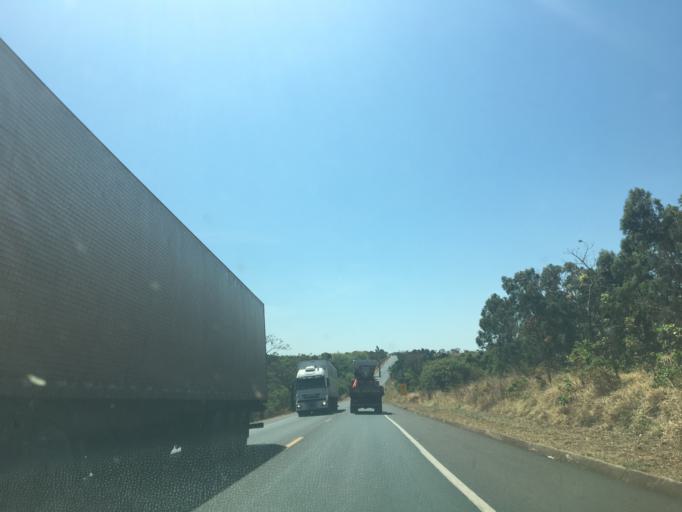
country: BR
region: Minas Gerais
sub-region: Monte Alegre De Minas
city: Monte Alegre de Minas
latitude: -18.9065
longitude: -49.0396
